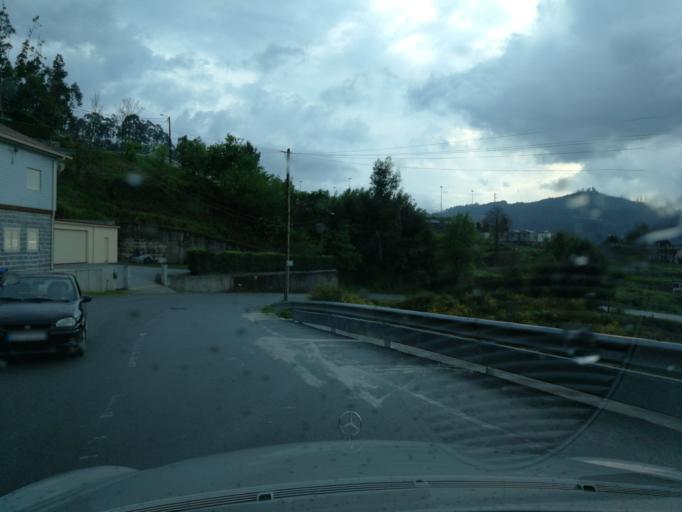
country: PT
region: Braga
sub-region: Vila Nova de Famalicao
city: Joane
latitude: 41.4781
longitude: -8.4240
